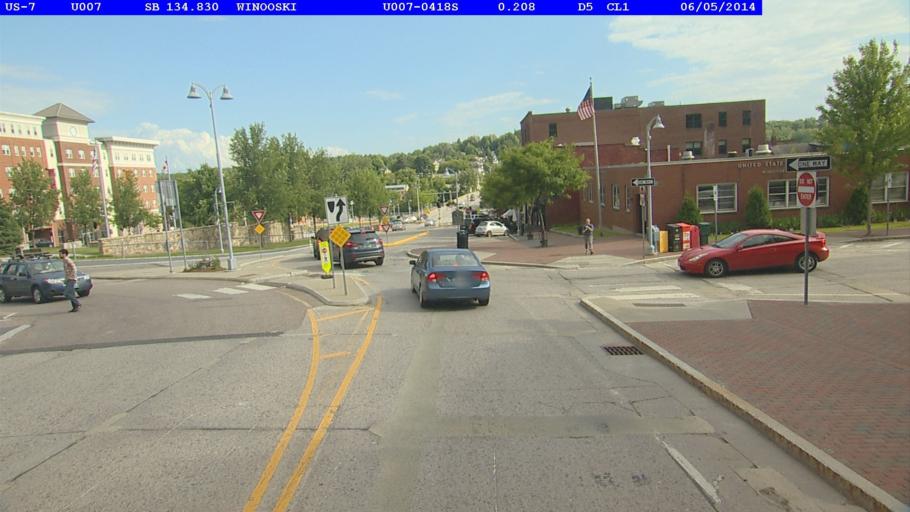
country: US
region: Vermont
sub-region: Chittenden County
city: Winooski
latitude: 44.4915
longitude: -73.1865
